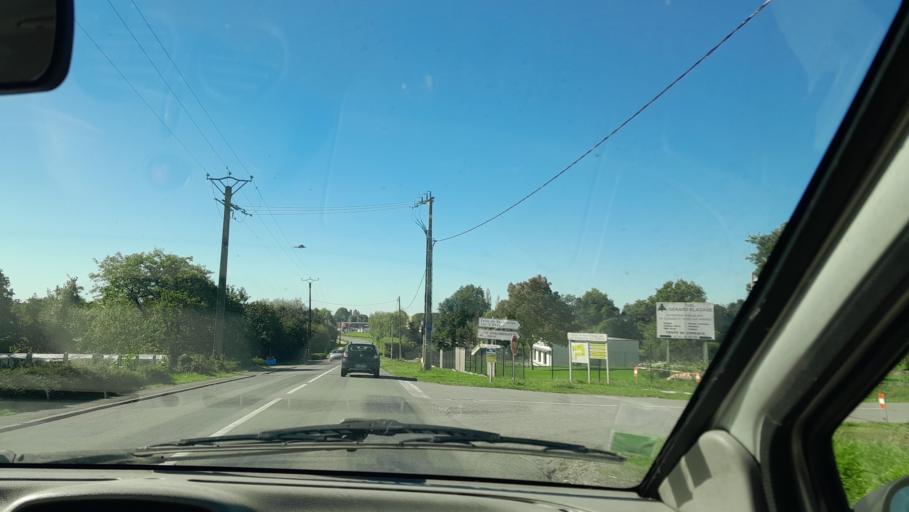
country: FR
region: Pays de la Loire
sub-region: Departement de la Mayenne
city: Loiron
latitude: 48.0693
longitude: -0.9308
